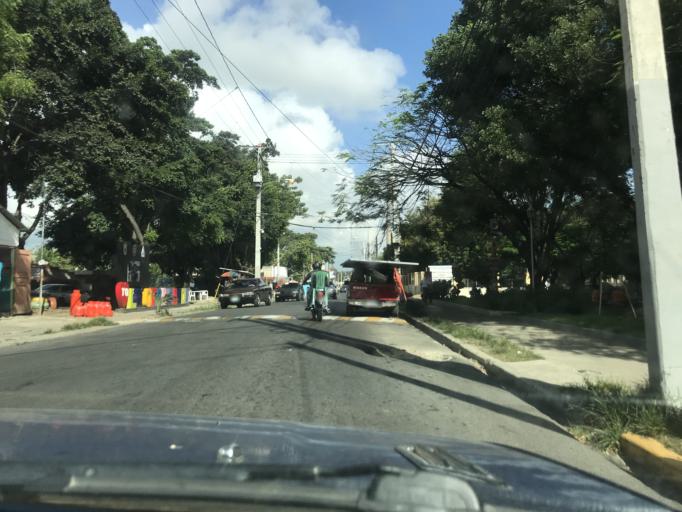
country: DO
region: Santiago
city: Santiago de los Caballeros
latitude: 19.4545
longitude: -70.7175
